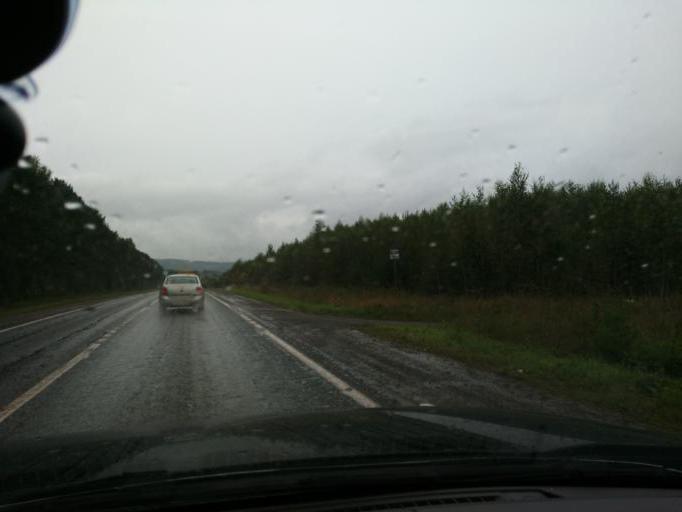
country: RU
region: Perm
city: Yugo-Kamskiy
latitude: 57.6772
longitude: 55.5784
